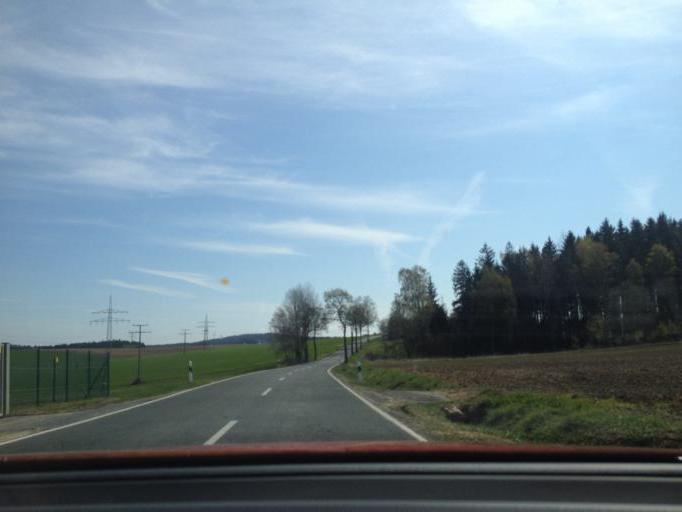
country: DE
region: Bavaria
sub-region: Upper Franconia
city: Roslau
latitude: 50.0796
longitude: 12.0003
